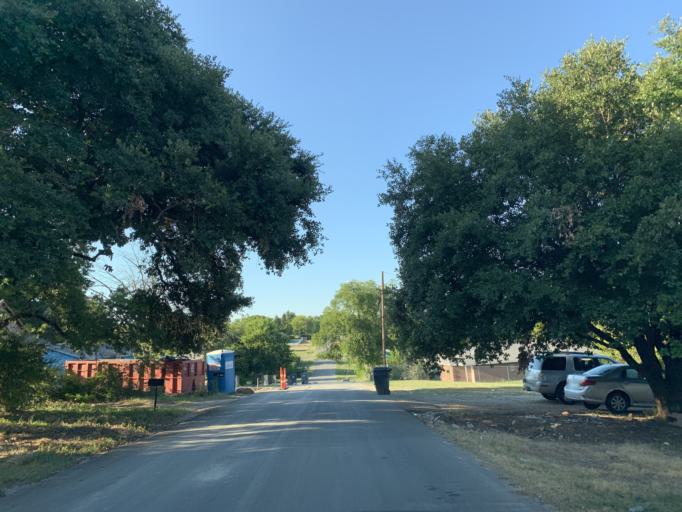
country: US
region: Texas
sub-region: Dallas County
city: Hutchins
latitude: 32.6681
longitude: -96.7782
